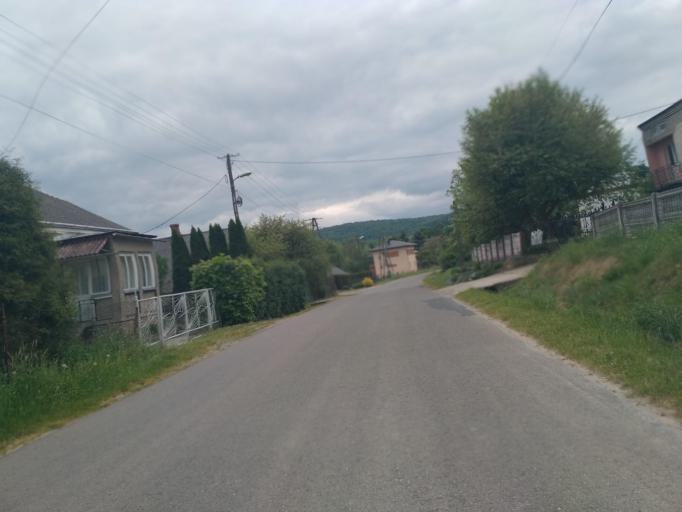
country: PL
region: Subcarpathian Voivodeship
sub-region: Powiat krosnienski
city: Jedlicze
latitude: 49.6971
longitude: 21.6397
